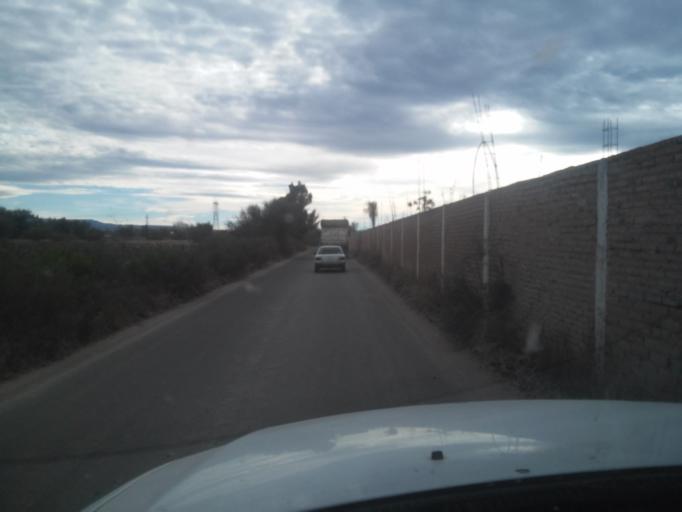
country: MX
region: Durango
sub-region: Durango
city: Jose Refugio Salcido
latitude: 24.0322
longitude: -104.5658
